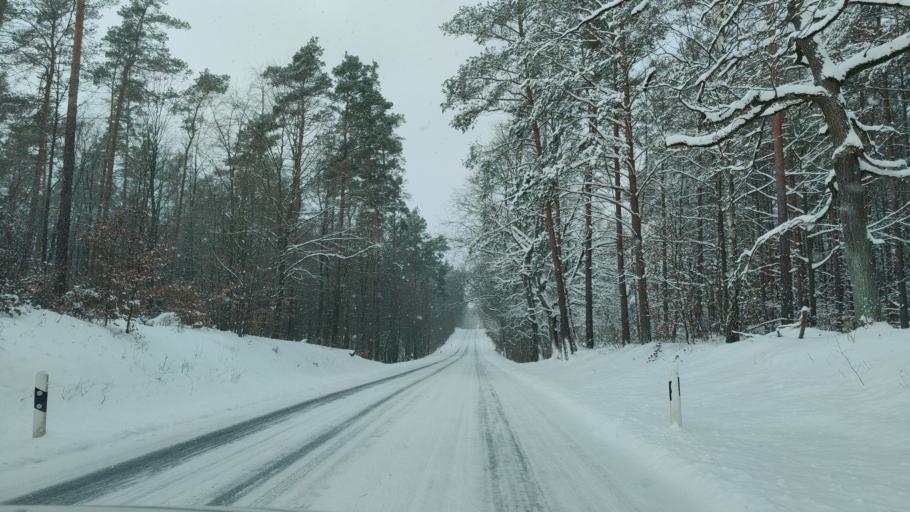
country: DE
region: Saxony
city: Bad Duben
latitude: 51.6522
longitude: 12.6005
